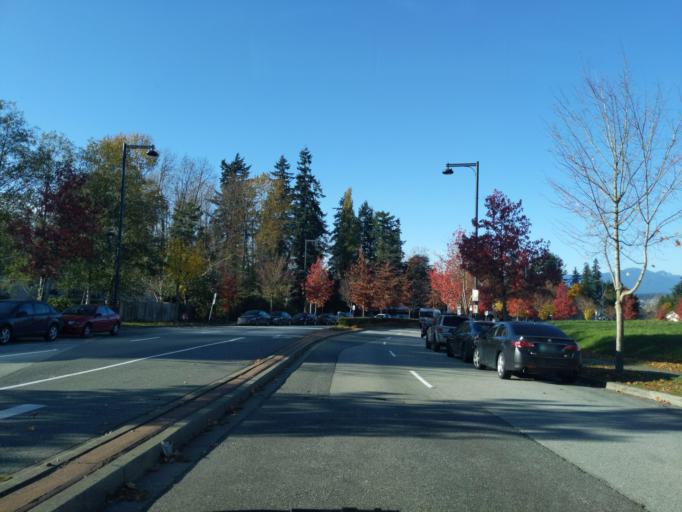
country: CA
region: British Columbia
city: New Westminster
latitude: 49.2005
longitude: -122.8516
